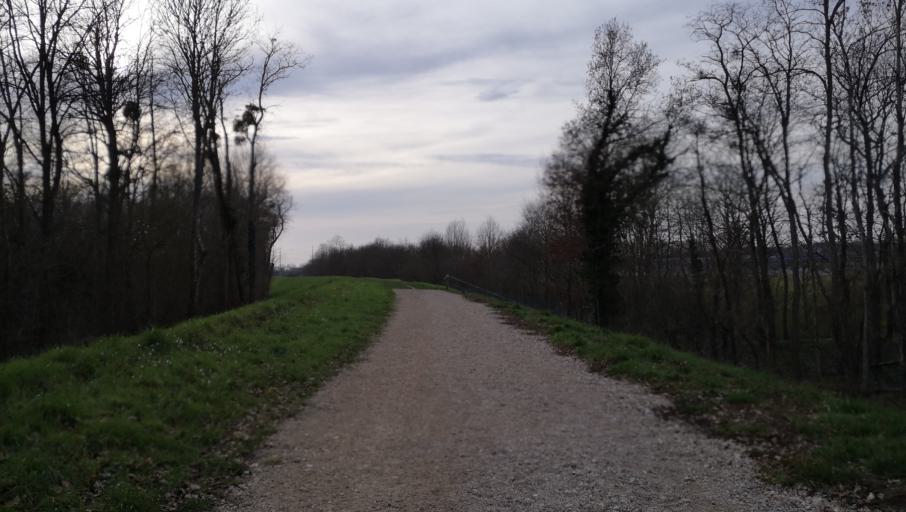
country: FR
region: Centre
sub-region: Departement du Loiret
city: Saint-Hilaire-Saint-Mesmin
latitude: 47.8726
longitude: 1.8151
